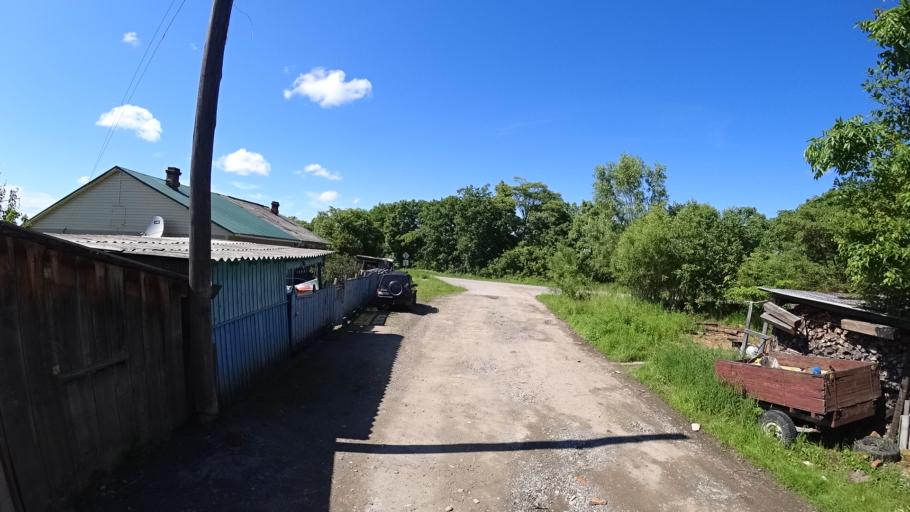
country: RU
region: Khabarovsk Krai
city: Khor
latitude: 47.8889
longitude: 135.0249
